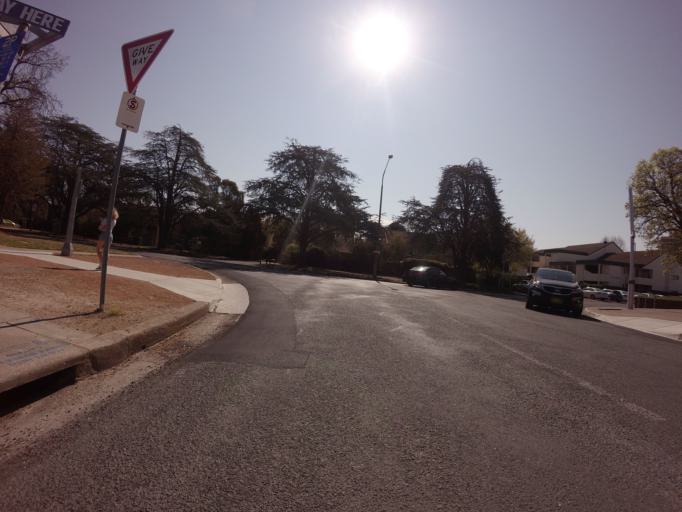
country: AU
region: Australian Capital Territory
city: Forrest
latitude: -35.3162
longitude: 149.1400
